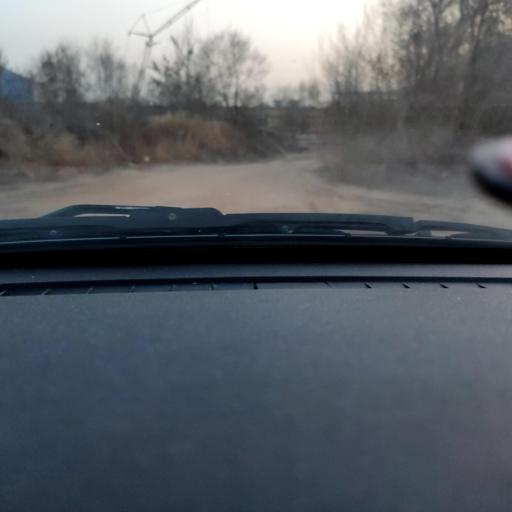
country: RU
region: Voronezj
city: Voronezh
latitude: 51.6877
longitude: 39.1426
